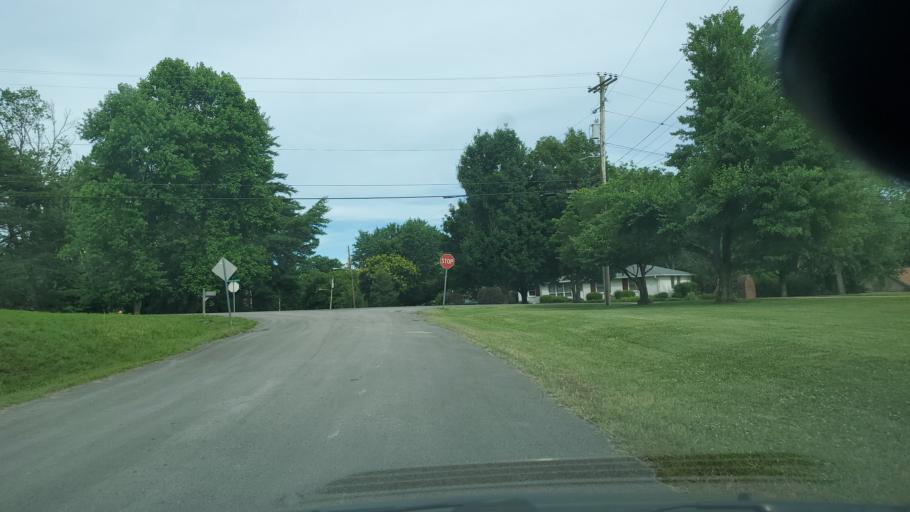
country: US
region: Tennessee
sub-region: Davidson County
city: Lakewood
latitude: 36.2219
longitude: -86.6861
